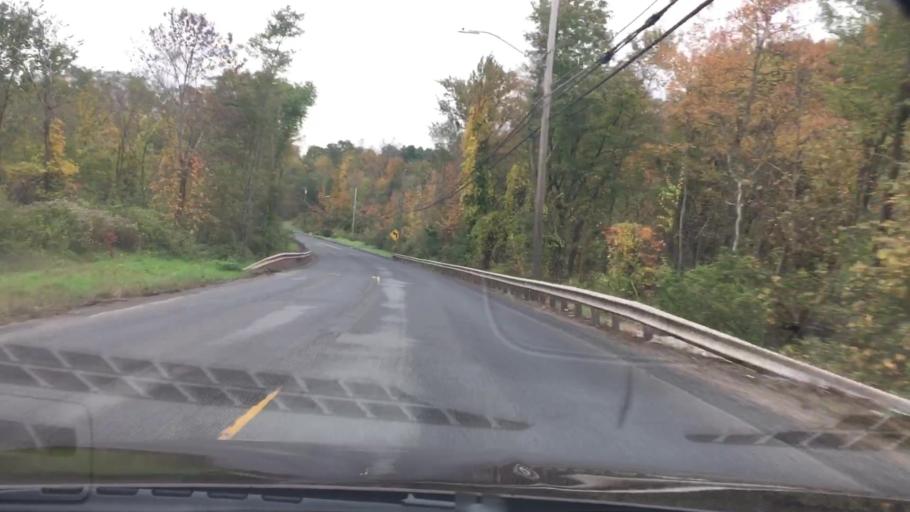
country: US
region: Connecticut
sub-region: Hartford County
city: Broad Brook
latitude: 41.9282
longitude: -72.5515
